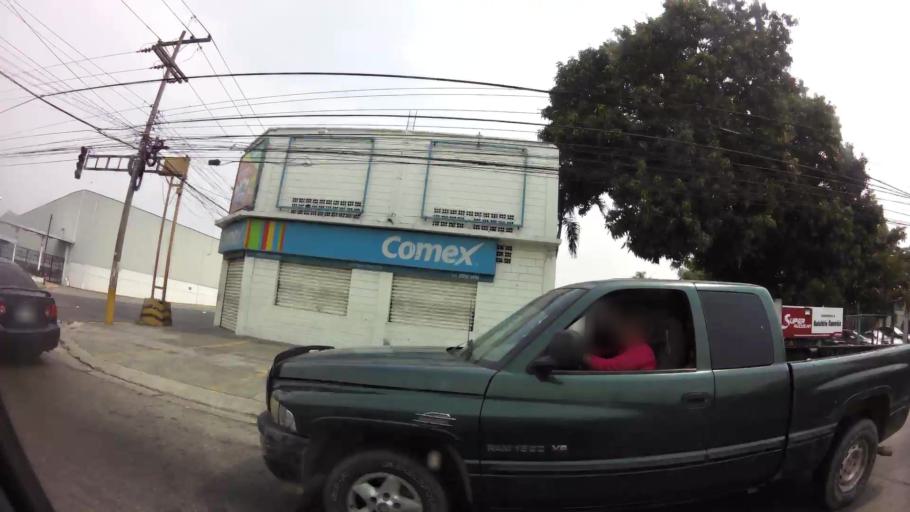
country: HN
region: Cortes
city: San Pedro Sula
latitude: 15.4908
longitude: -88.0296
